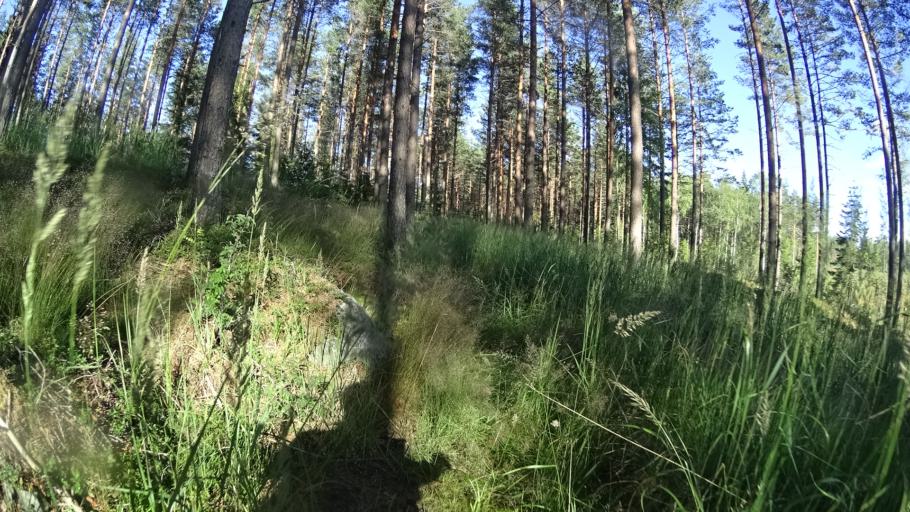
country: FI
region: Uusimaa
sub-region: Helsinki
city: Karkkila
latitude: 60.6505
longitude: 24.1563
